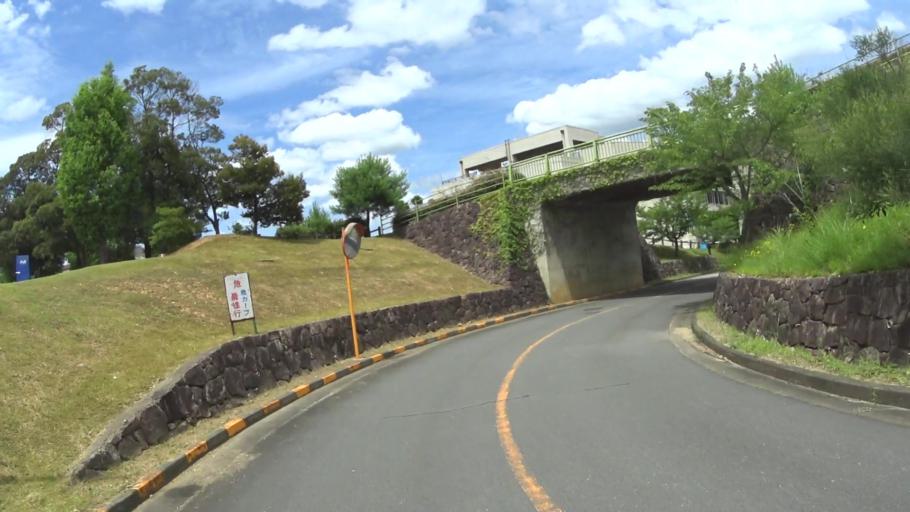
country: JP
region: Kyoto
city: Ayabe
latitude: 35.1669
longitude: 135.4160
